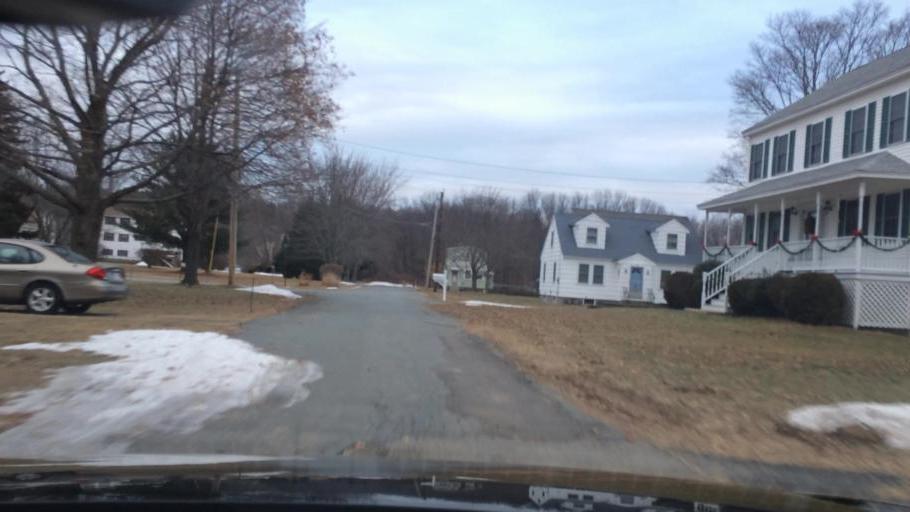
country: US
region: Massachusetts
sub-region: Essex County
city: North Andover
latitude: 42.7370
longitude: -71.1271
